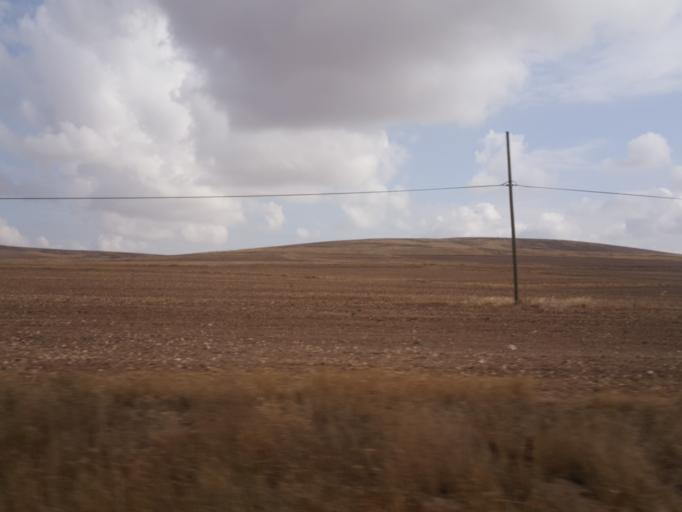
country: TR
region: Kirikkale
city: Keskin
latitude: 39.6301
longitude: 33.6098
